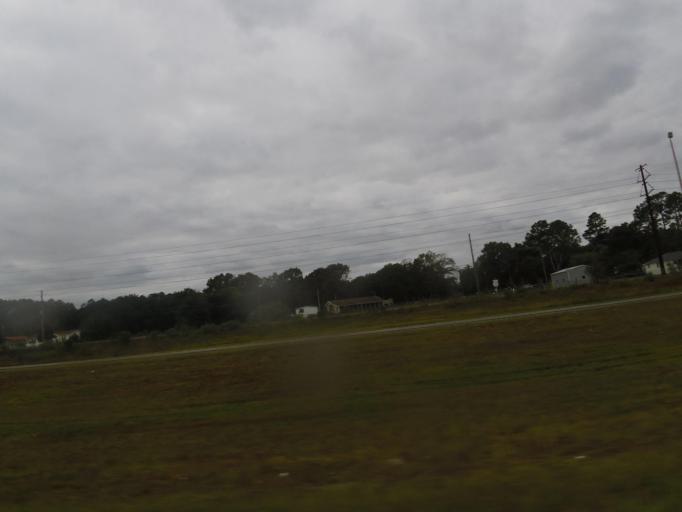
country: US
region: Florida
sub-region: Clay County
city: Lakeside
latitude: 30.1419
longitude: -81.8307
